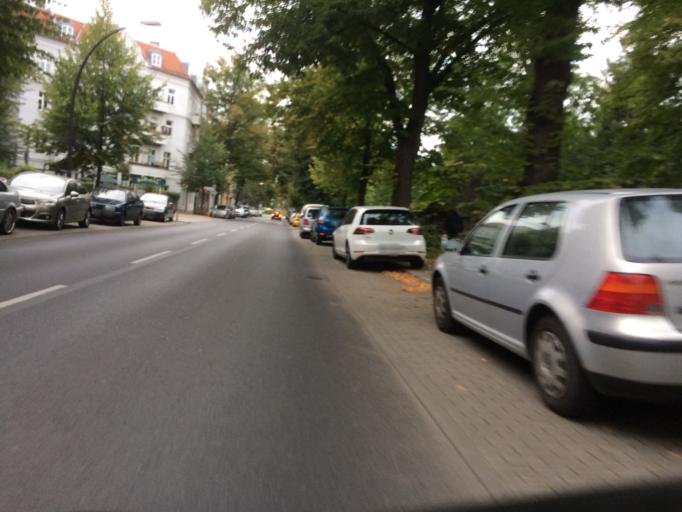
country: DE
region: Berlin
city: Heinersdorf
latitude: 52.5547
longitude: 13.4424
